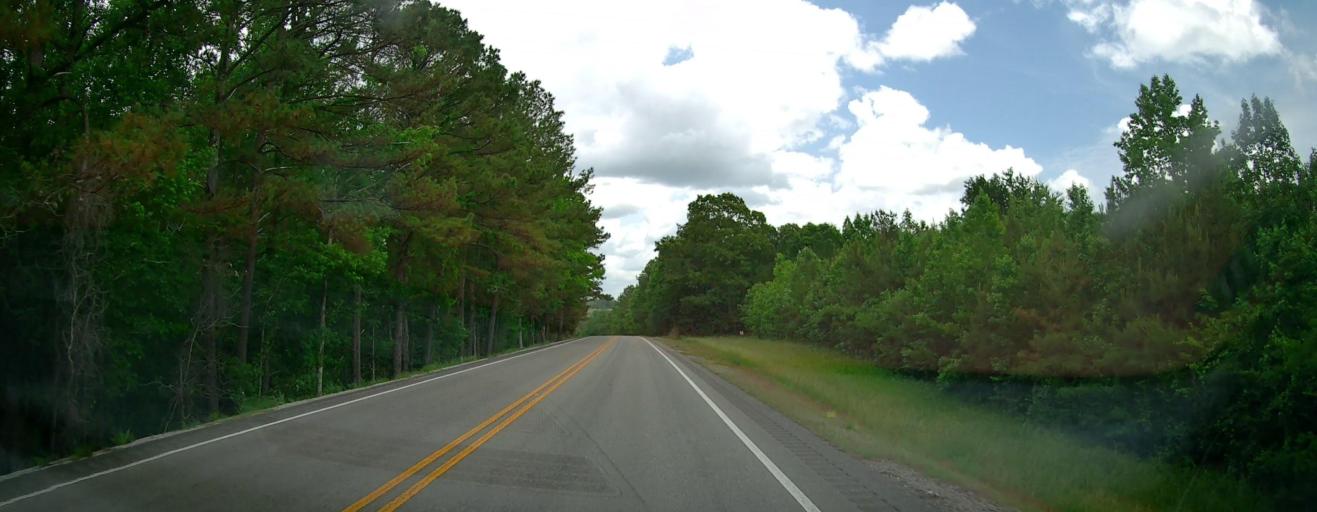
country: US
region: Alabama
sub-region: Marion County
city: Hamilton
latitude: 34.1247
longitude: -88.0360
